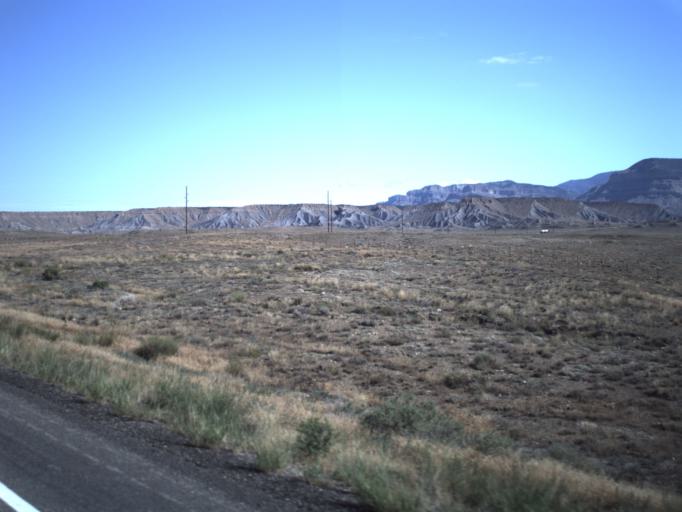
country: US
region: Utah
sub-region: Carbon County
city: East Carbon City
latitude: 39.3668
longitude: -110.3941
